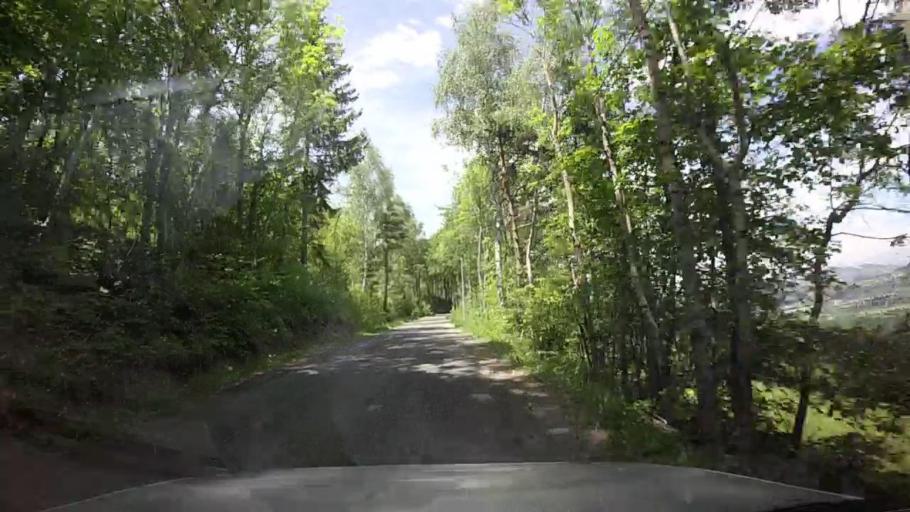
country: FR
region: Provence-Alpes-Cote d'Azur
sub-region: Departement des Alpes-de-Haute-Provence
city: Seyne-les-Alpes
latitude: 44.3332
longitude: 6.3448
